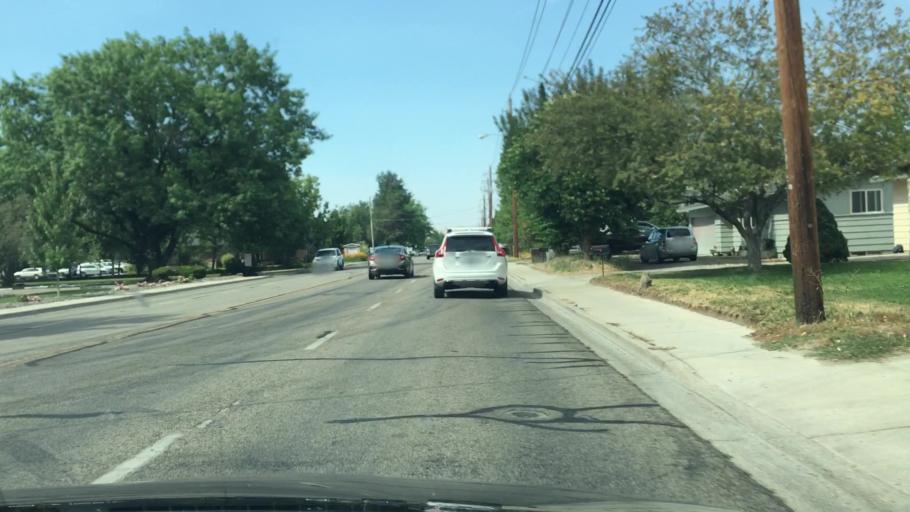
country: US
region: Idaho
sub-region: Ada County
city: Garden City
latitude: 43.6304
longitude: -116.2742
